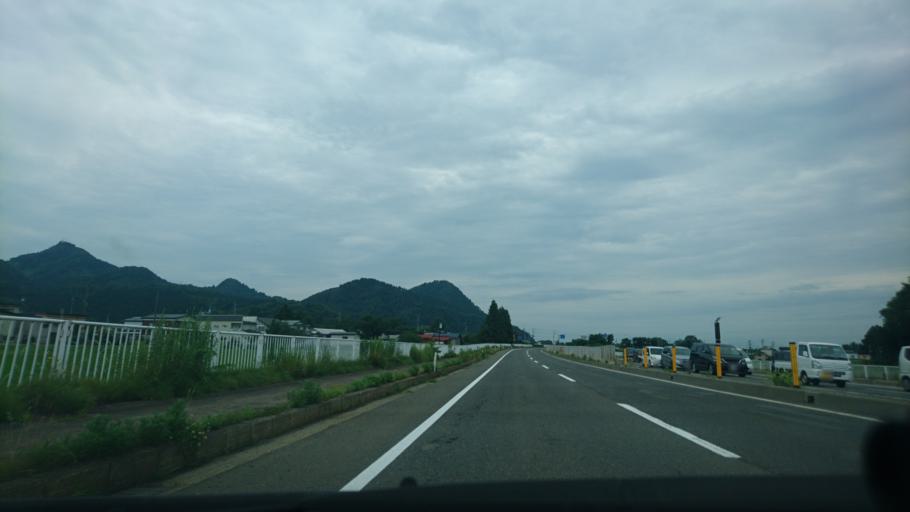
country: JP
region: Akita
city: Omagari
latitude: 39.4777
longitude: 140.4621
